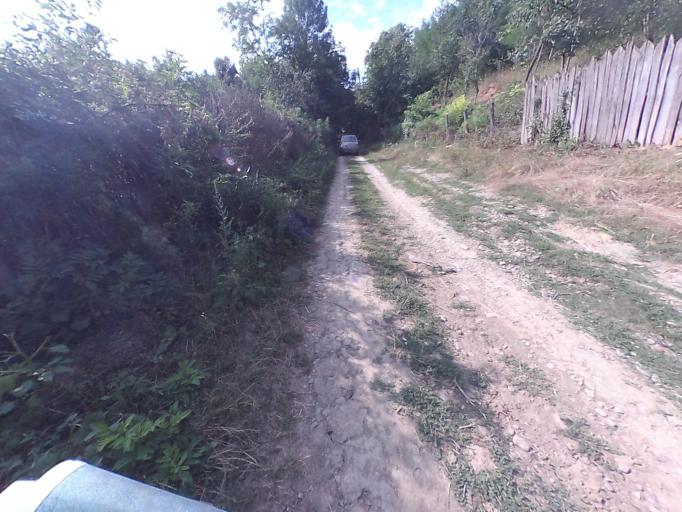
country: RO
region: Vaslui
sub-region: Comuna Osesti
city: Buda
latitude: 46.7595
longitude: 27.4093
